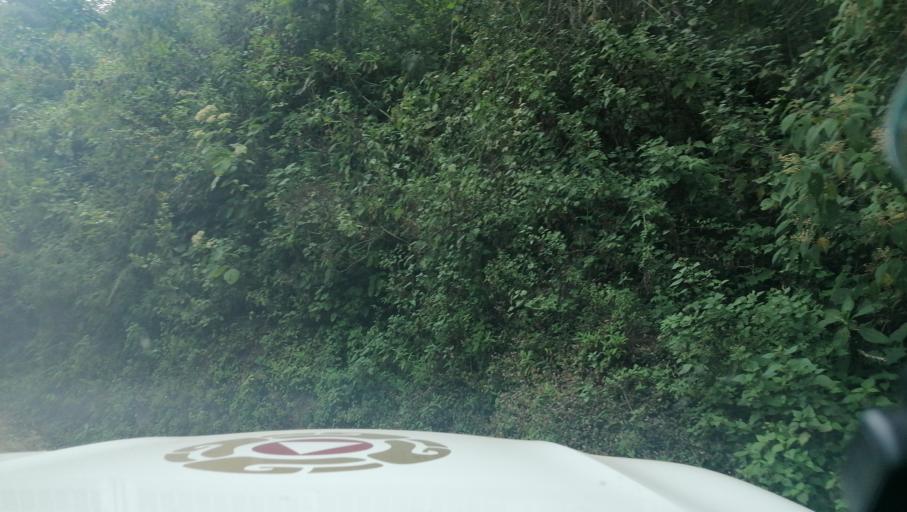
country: GT
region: San Marcos
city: Tacana
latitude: 15.2157
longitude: -92.1826
